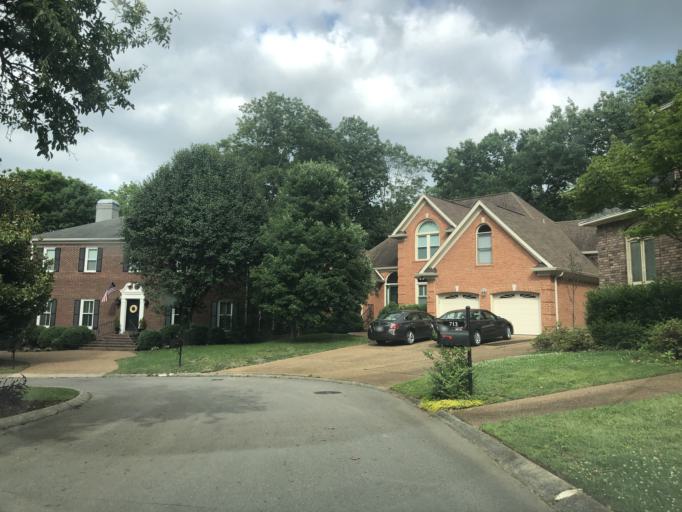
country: US
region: Tennessee
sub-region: Davidson County
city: Oak Hill
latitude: 36.0953
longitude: -86.8132
